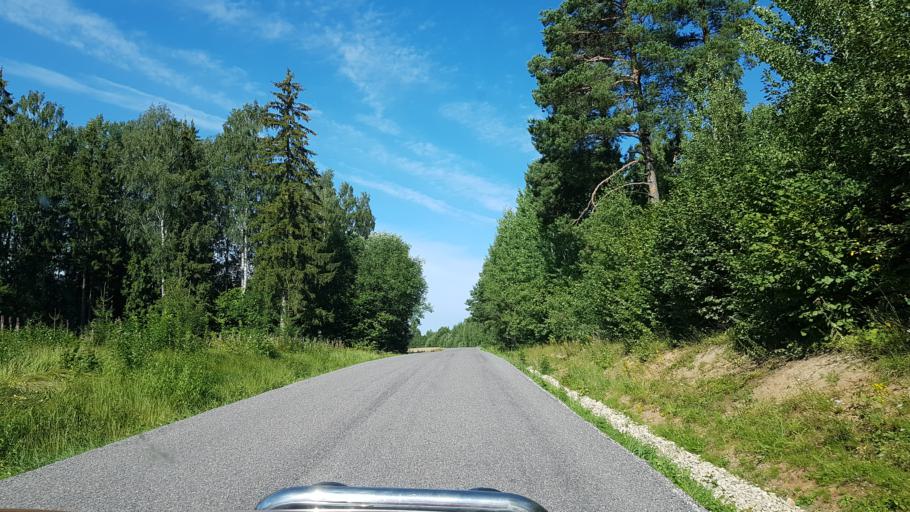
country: EE
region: Tartu
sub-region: Puhja vald
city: Puhja
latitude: 58.2536
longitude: 26.3292
